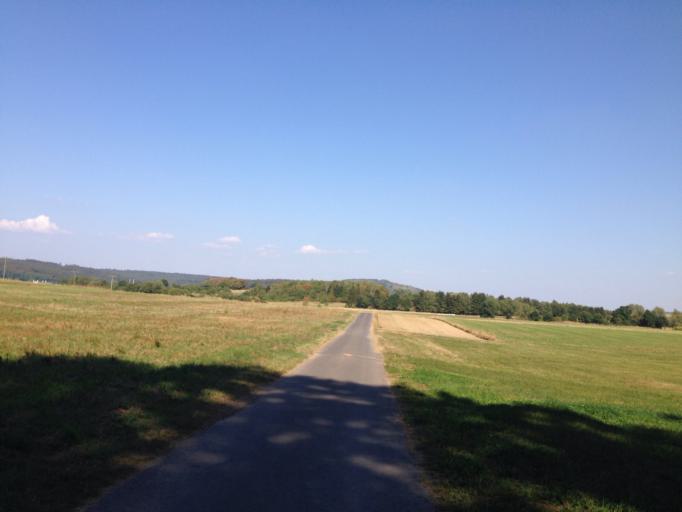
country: DE
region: Hesse
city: Staufenberg
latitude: 50.6493
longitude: 8.7504
